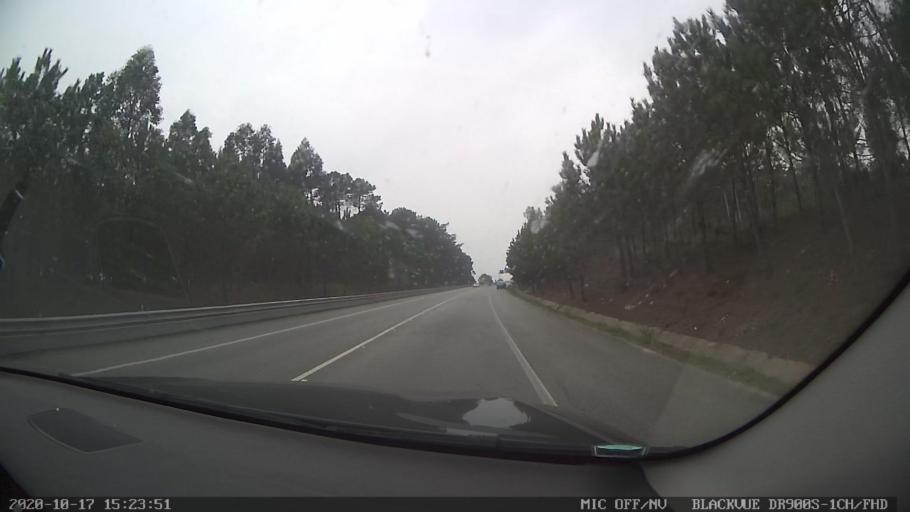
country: PT
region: Braga
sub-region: Esposende
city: Esposende
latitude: 41.5286
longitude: -8.7457
